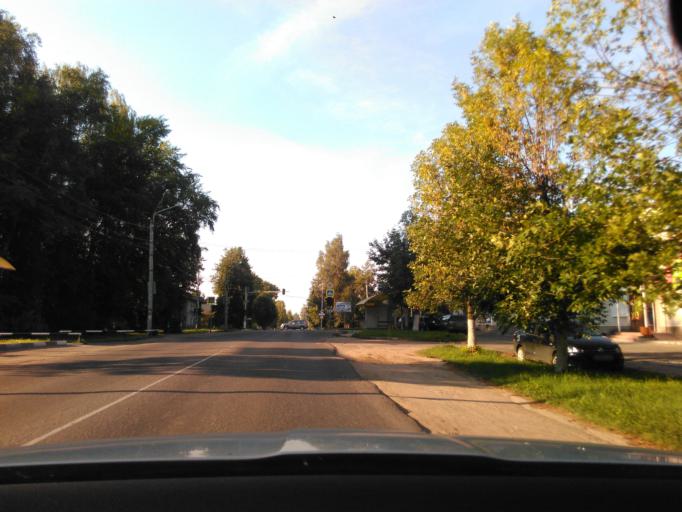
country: RU
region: Tverskaya
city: Konakovo
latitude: 56.6889
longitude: 36.7634
